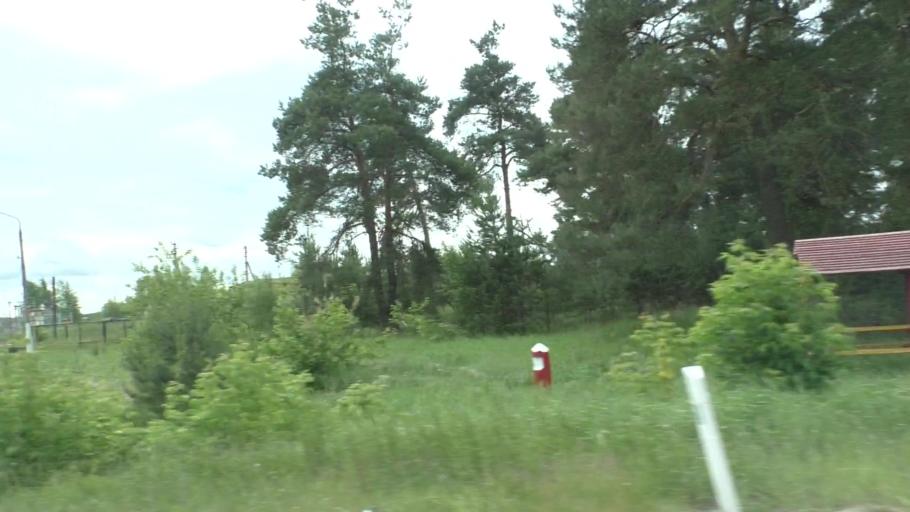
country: RU
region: Moskovskaya
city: Imeni Tsyurupy
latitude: 55.5081
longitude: 38.7592
